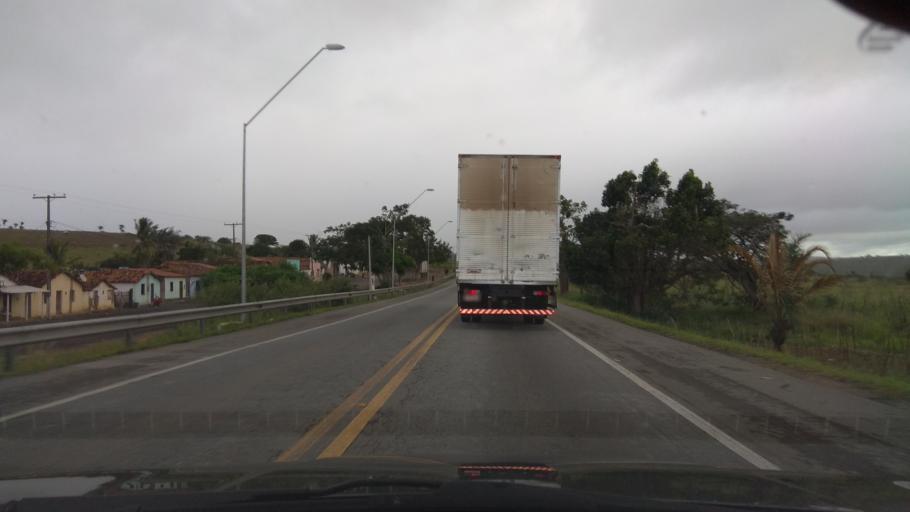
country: BR
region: Bahia
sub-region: Jaguaquara
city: Jaguaquara
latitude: -13.4809
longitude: -40.0423
